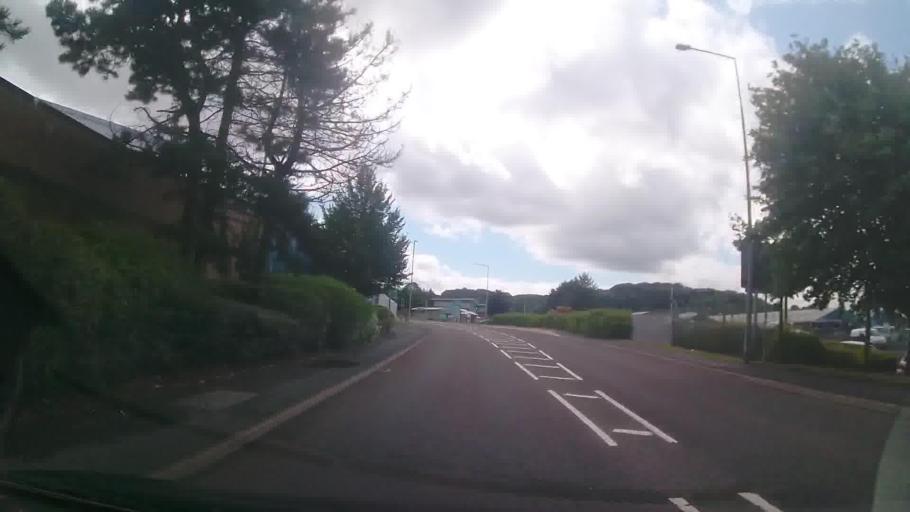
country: GB
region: England
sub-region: Telford and Wrekin
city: Oakengates
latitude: 52.7097
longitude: -2.4341
